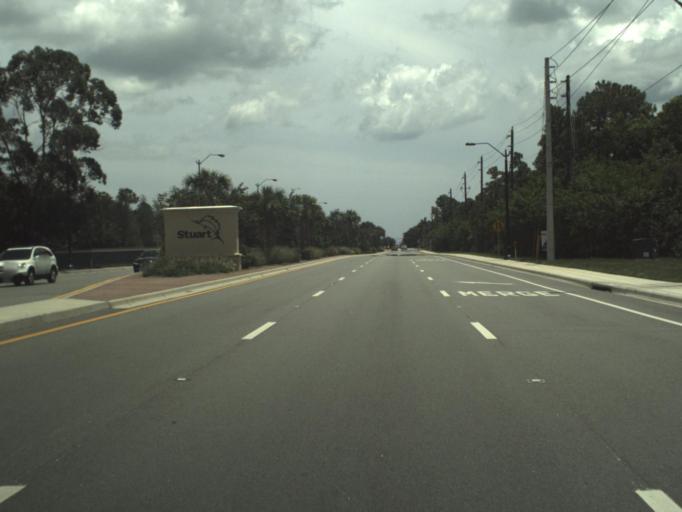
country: US
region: Florida
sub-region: Martin County
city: Palm City
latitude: 27.1587
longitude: -80.2456
